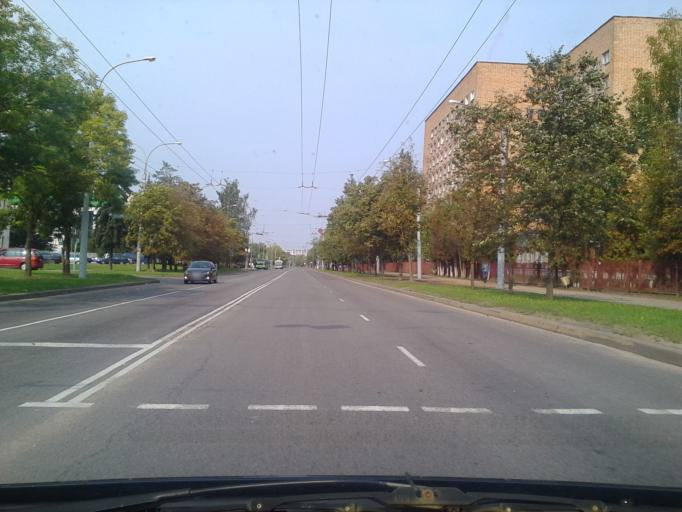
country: BY
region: Minsk
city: Syenitsa
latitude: 53.8582
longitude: 27.4980
